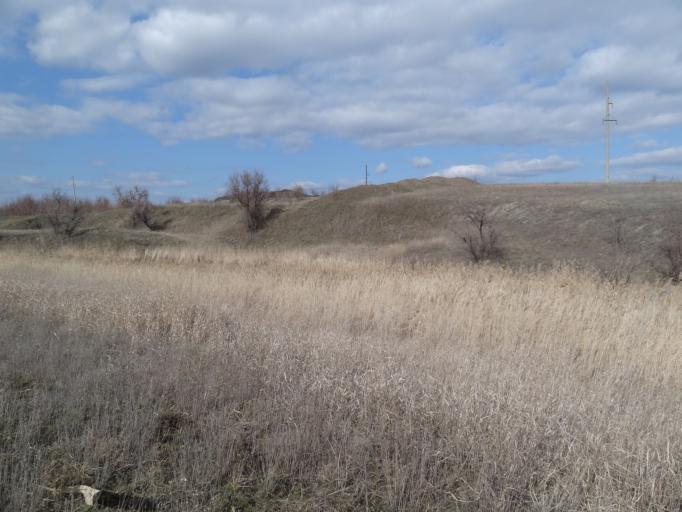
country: RU
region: Saratov
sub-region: Saratovskiy Rayon
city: Saratov
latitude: 51.6704
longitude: 46.0206
